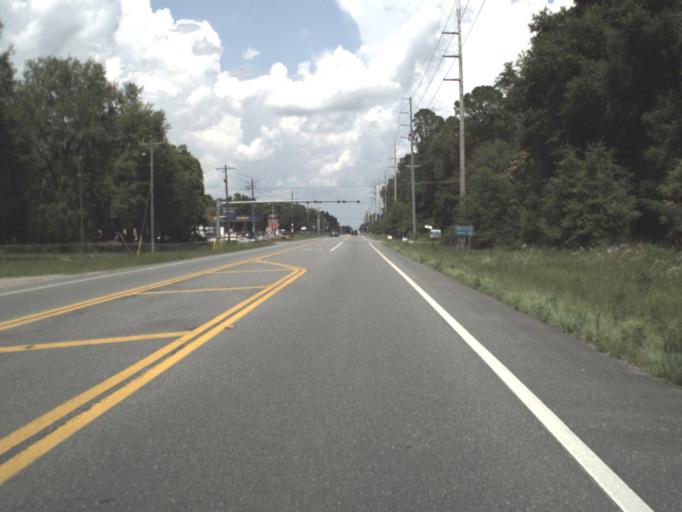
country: US
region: Florida
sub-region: Alachua County
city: Newberry
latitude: 29.6343
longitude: -82.6918
